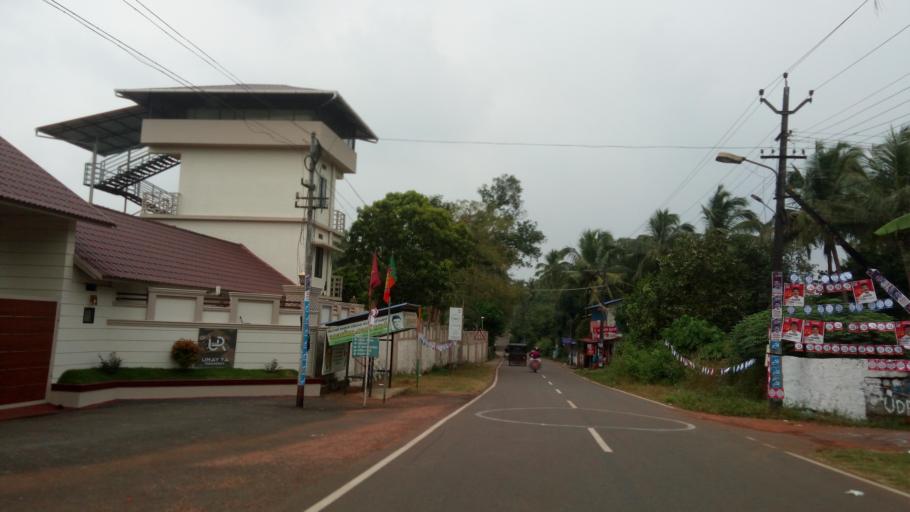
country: IN
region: Kerala
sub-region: Malappuram
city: Malappuram
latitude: 10.9853
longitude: 76.0071
